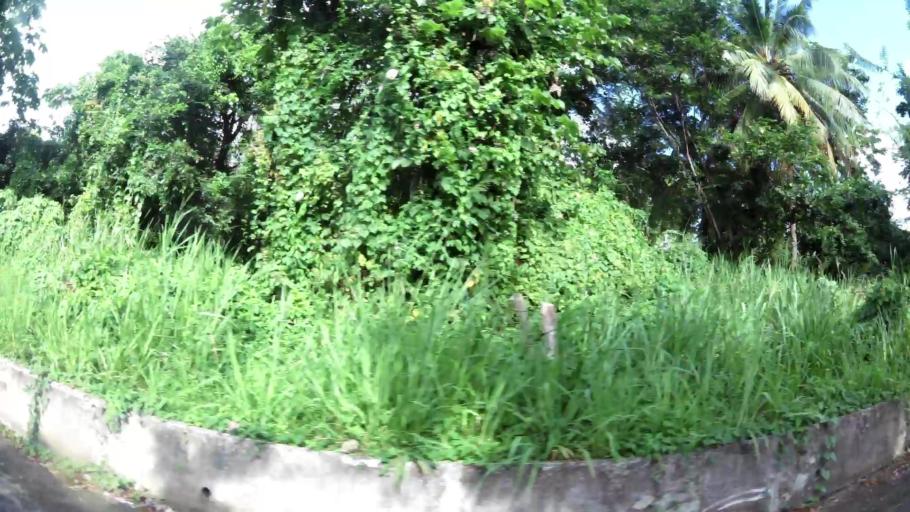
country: MQ
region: Martinique
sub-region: Martinique
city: Ducos
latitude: 14.5555
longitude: -60.9614
